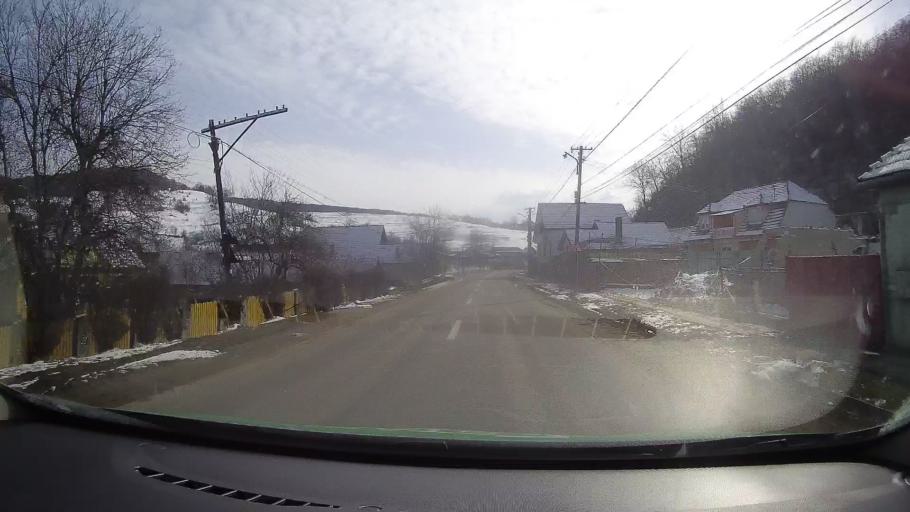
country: RO
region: Mures
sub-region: Municipiul Sighisoara
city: Sighisoara
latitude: 46.2063
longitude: 24.7779
